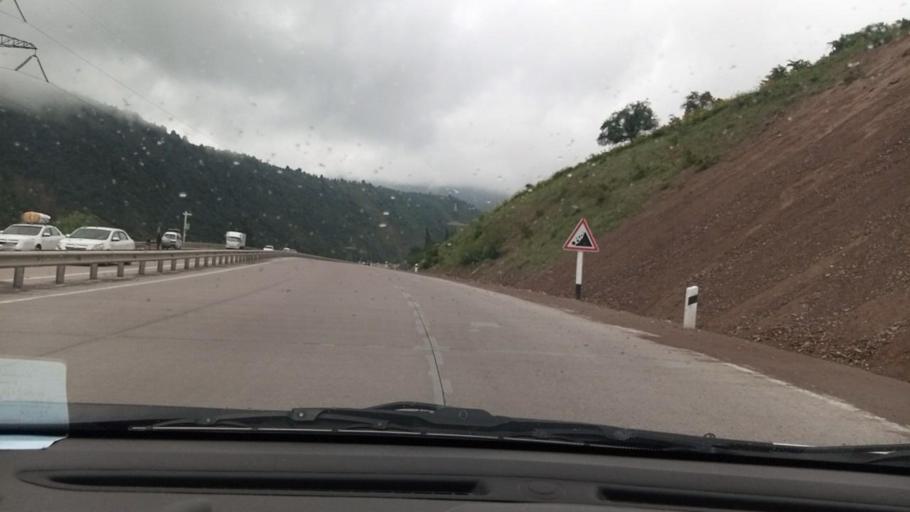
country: UZ
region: Toshkent
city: Angren
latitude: 41.1382
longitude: 70.4586
